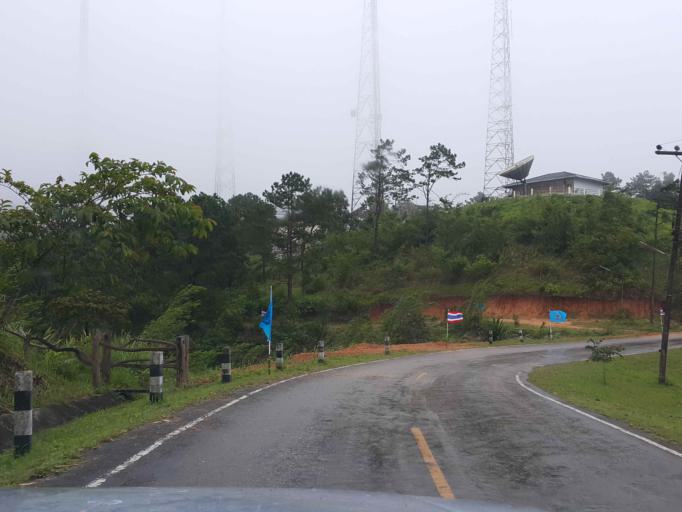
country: TH
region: Tak
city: Tak
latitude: 16.7771
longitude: 98.9283
